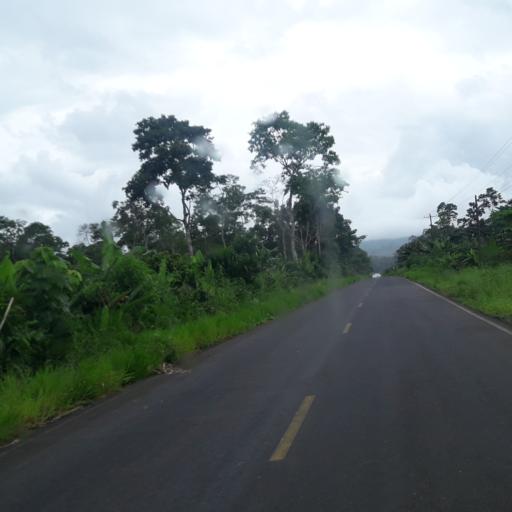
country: EC
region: Napo
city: Tena
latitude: -1.0471
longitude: -77.6637
